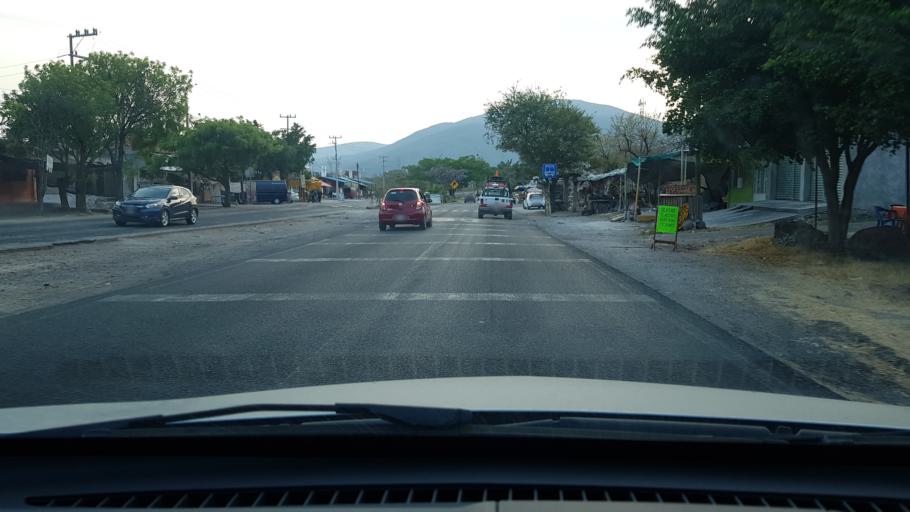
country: MX
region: Morelos
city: Yautepec
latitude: 18.8658
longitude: -99.0903
